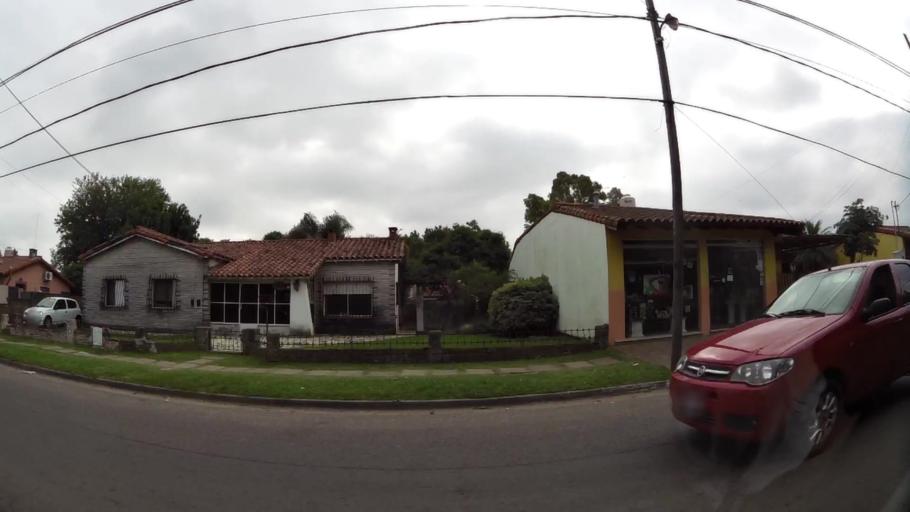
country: AR
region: Buenos Aires
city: San Justo
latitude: -34.7295
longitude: -58.5348
